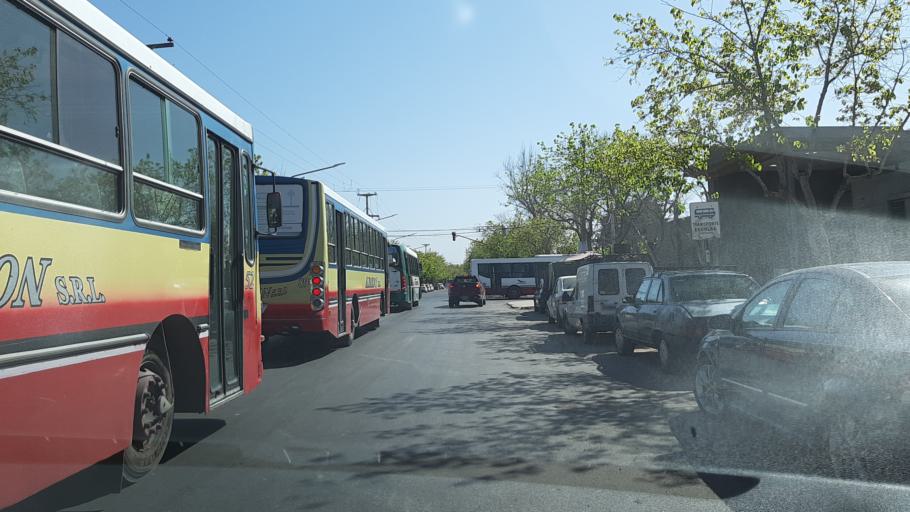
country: AR
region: San Juan
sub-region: Departamento de Santa Lucia
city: Santa Lucia
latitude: -31.5409
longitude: -68.5116
